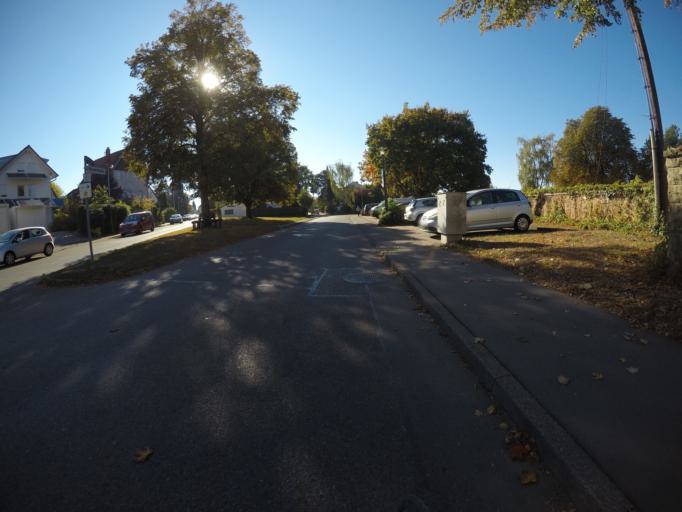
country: DE
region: Baden-Wuerttemberg
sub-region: Regierungsbezirk Stuttgart
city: Filderstadt
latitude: 48.6489
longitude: 9.2192
